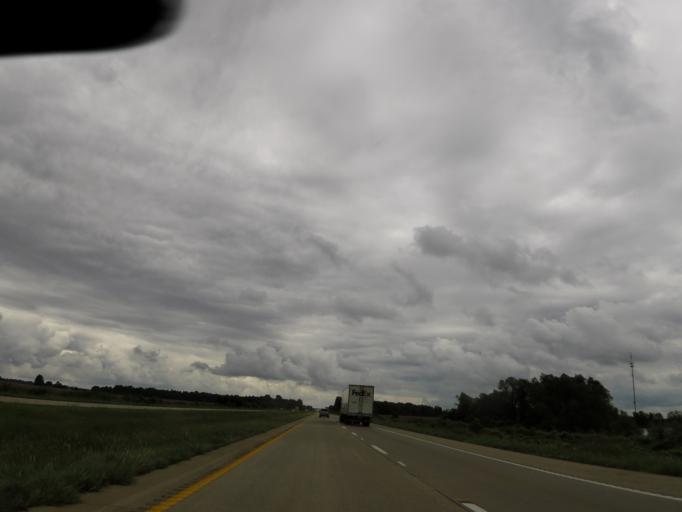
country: US
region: Missouri
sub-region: Mississippi County
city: Charleston
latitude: 36.9348
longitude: -89.3025
